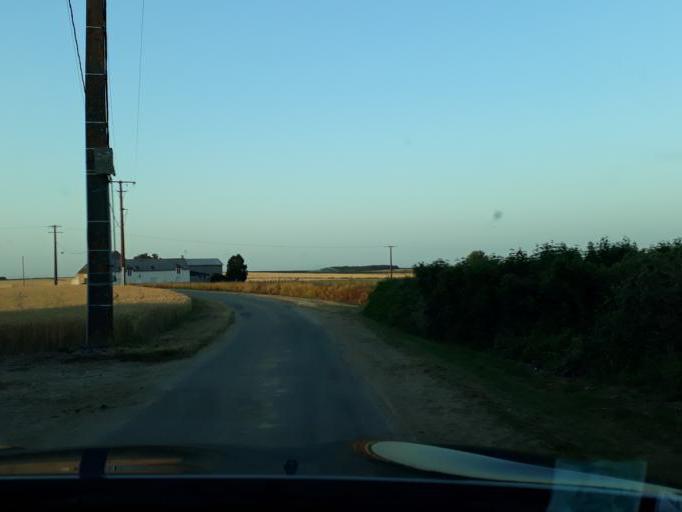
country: FR
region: Centre
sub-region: Departement du Loir-et-Cher
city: Ouzouer-le-Marche
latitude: 47.8580
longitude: 1.5538
